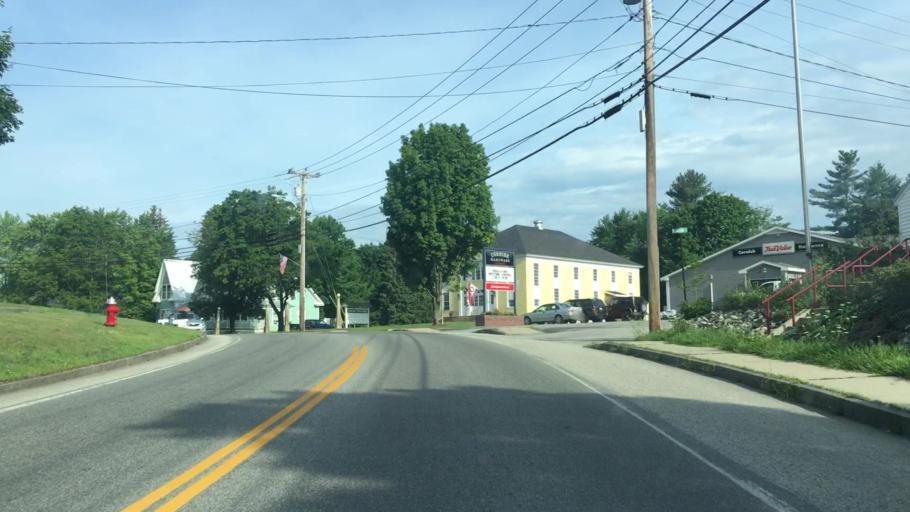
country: US
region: Maine
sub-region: York County
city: Cornish
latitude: 43.8053
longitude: -70.8049
